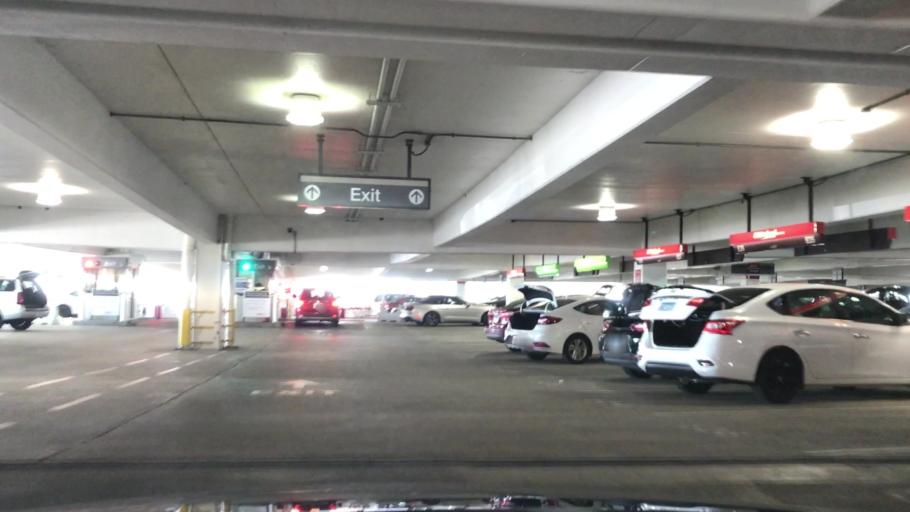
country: US
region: Louisiana
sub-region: Jefferson Parish
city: Kenner
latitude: 29.9847
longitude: -90.2604
